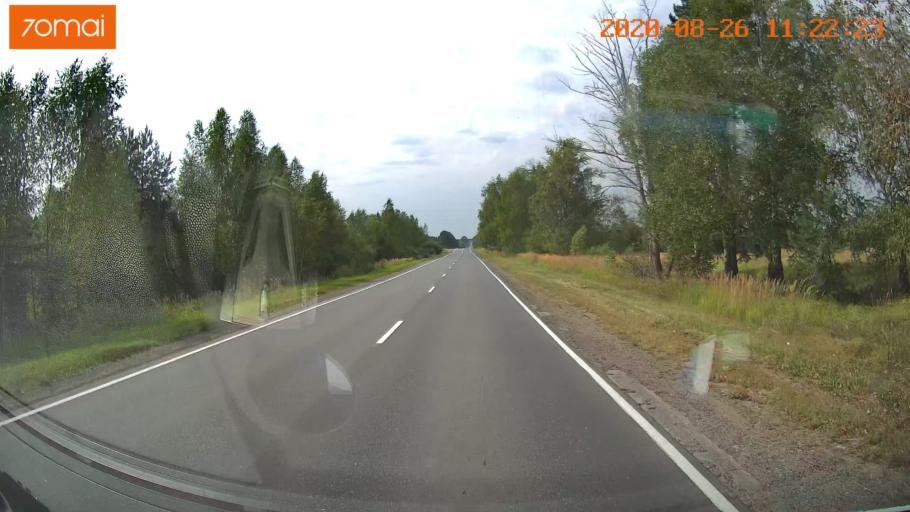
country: RU
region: Rjazan
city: Shilovo
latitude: 54.3645
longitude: 41.0281
